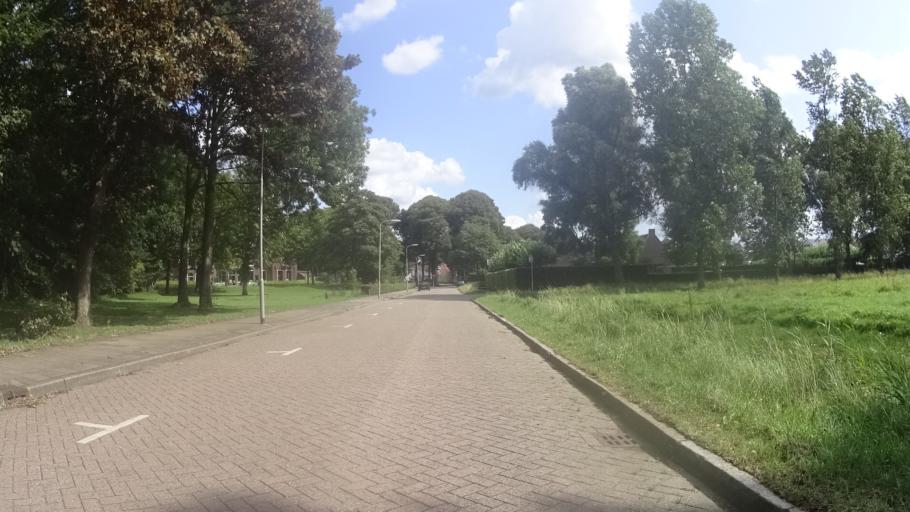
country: NL
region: North Holland
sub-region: Gemeente Beverwijk
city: Beverwijk
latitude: 52.4828
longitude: 4.6423
